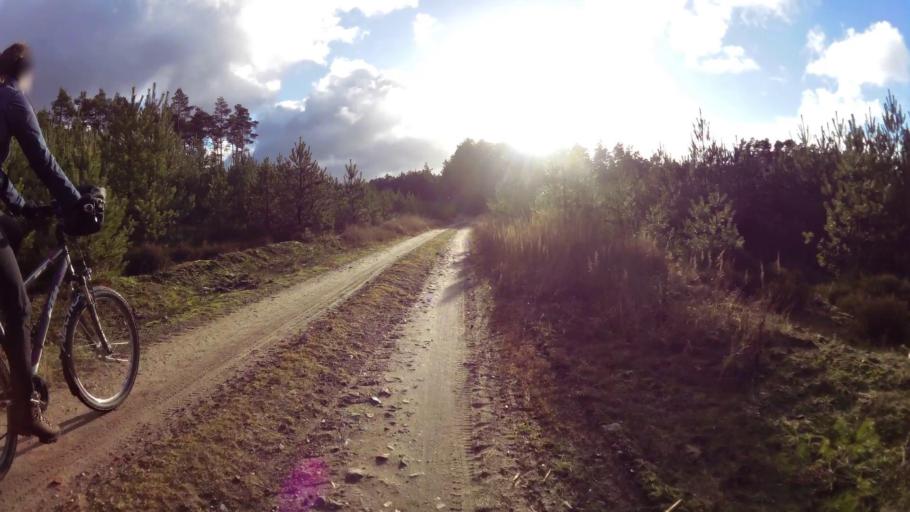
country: PL
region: West Pomeranian Voivodeship
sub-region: Powiat koszalinski
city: Sianow
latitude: 54.0943
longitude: 16.2938
